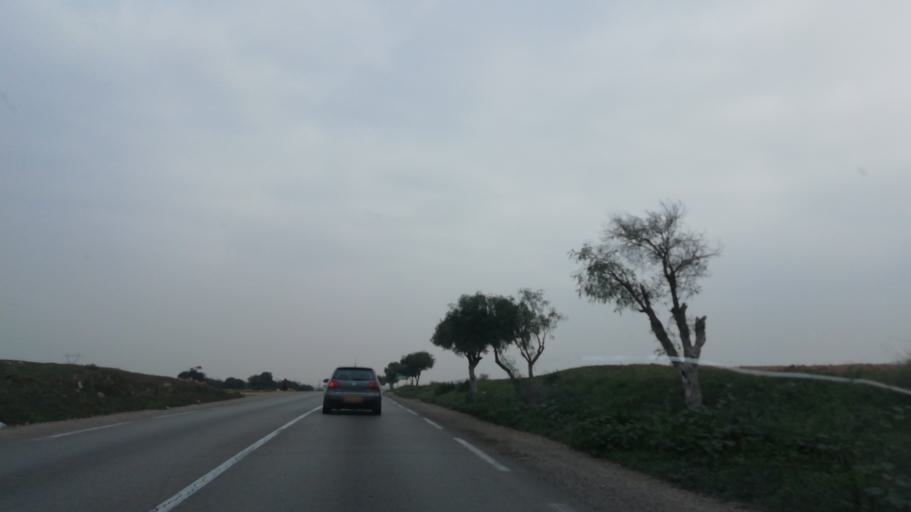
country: DZ
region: Mascara
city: Sig
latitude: 35.5462
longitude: -0.3004
